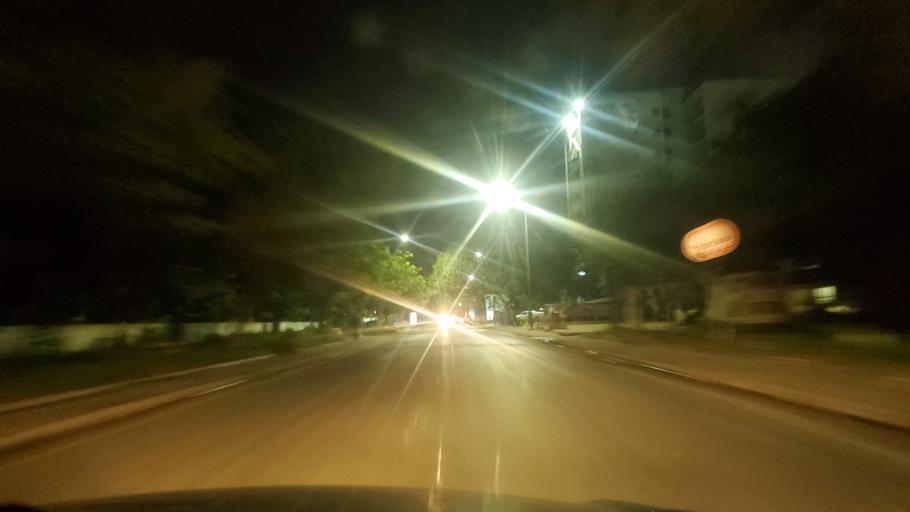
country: SN
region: Dakar
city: Mermoz Boabab
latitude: 14.7016
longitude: -17.4650
